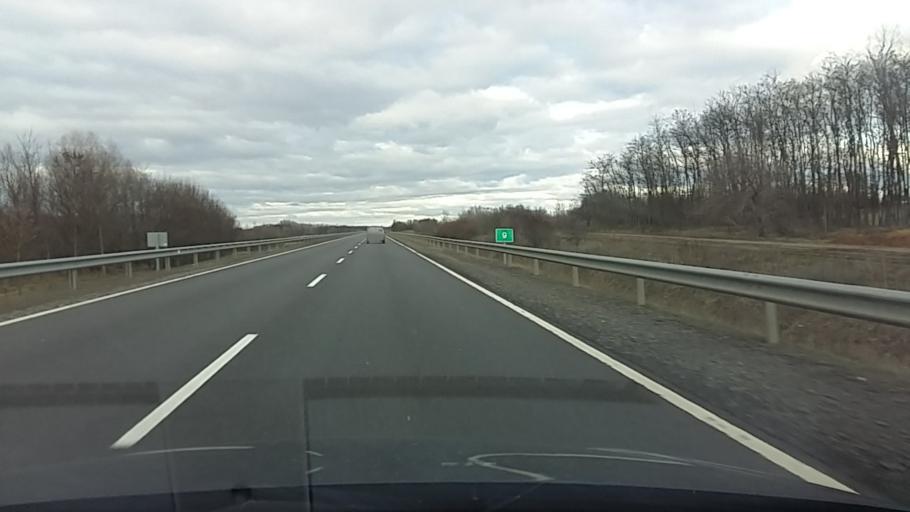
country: HU
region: Szabolcs-Szatmar-Bereg
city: Nyirpazony
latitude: 47.9726
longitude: 21.8173
